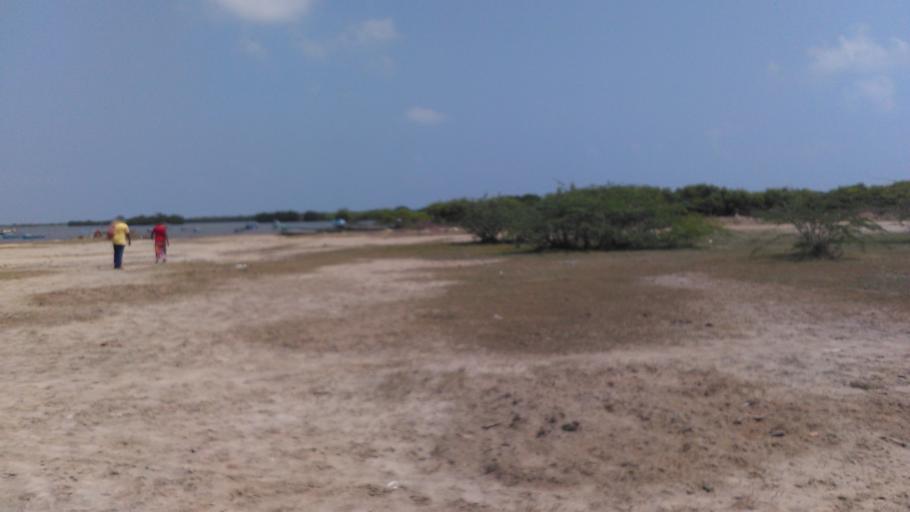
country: IN
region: Tamil Nadu
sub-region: Cuddalore
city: Annamalainagar
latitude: 11.4365
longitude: 79.7833
